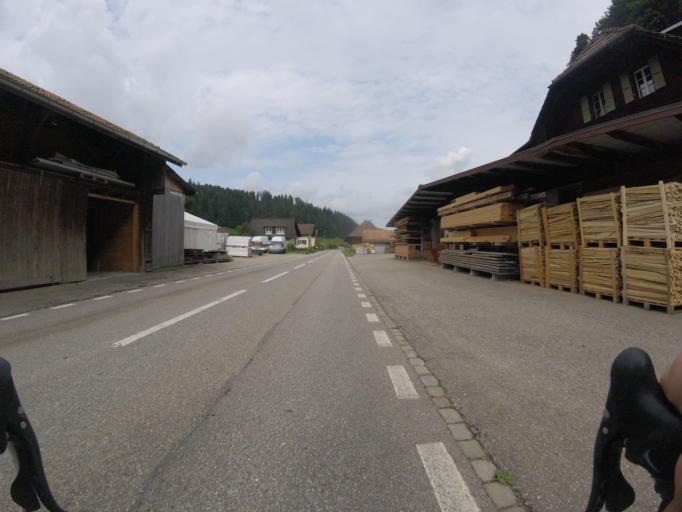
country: CH
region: Bern
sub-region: Emmental District
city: Lutzelfluh
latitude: 46.9946
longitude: 7.6836
